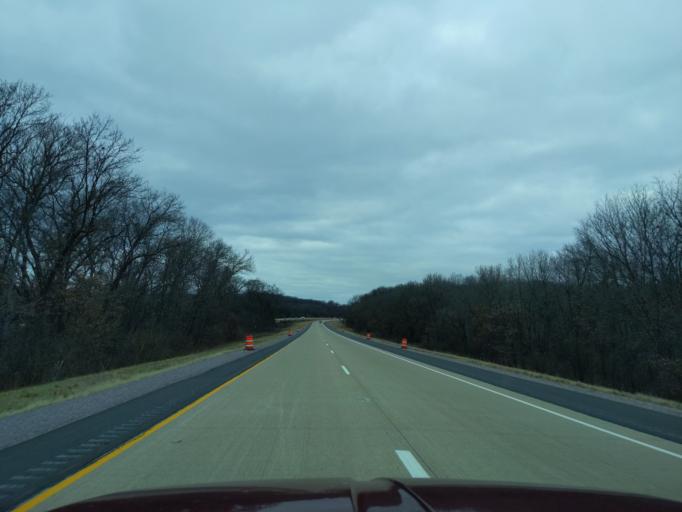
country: US
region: Wisconsin
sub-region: Columbia County
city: Portage
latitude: 43.6062
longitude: -89.4700
